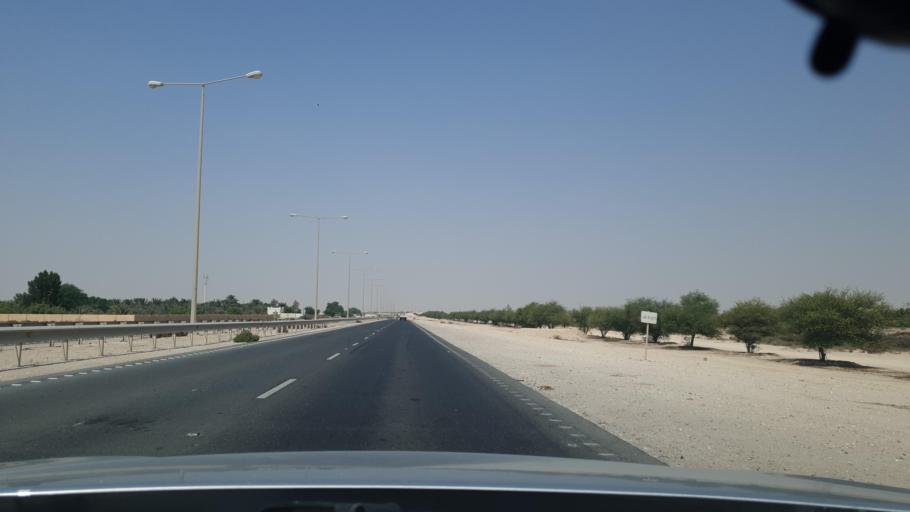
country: QA
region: Al Khawr
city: Al Khawr
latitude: 25.7262
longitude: 51.4967
